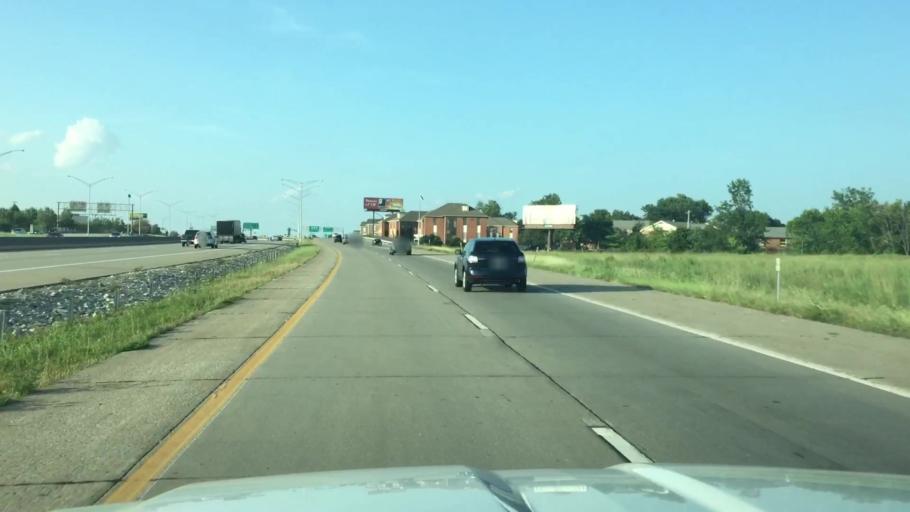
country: US
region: Missouri
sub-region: Saint Louis County
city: Mehlville
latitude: 38.5049
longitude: -90.3375
